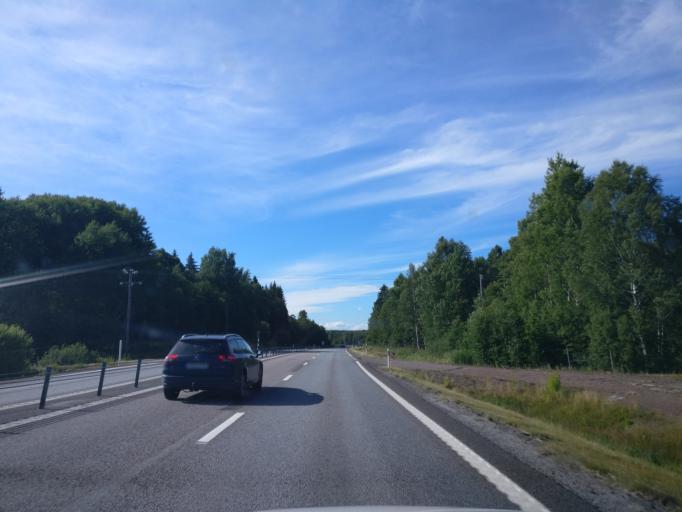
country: SE
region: Vaermland
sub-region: Kils Kommun
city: Kil
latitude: 59.4418
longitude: 13.3857
